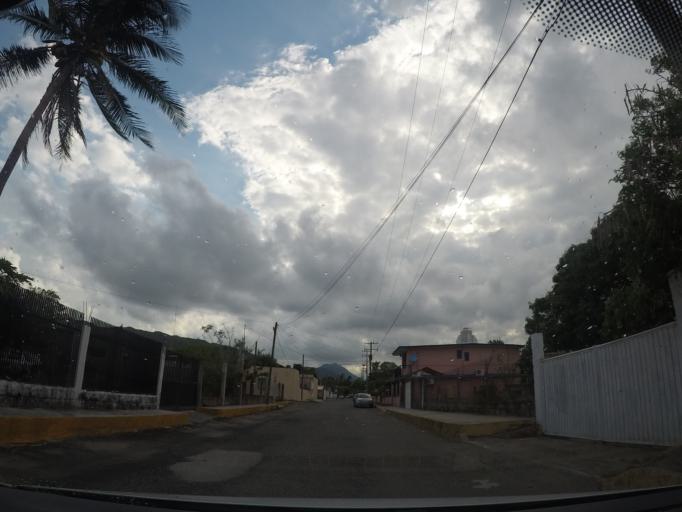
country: MX
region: Oaxaca
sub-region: Salina Cruz
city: Salina Cruz
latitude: 16.2094
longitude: -95.2083
